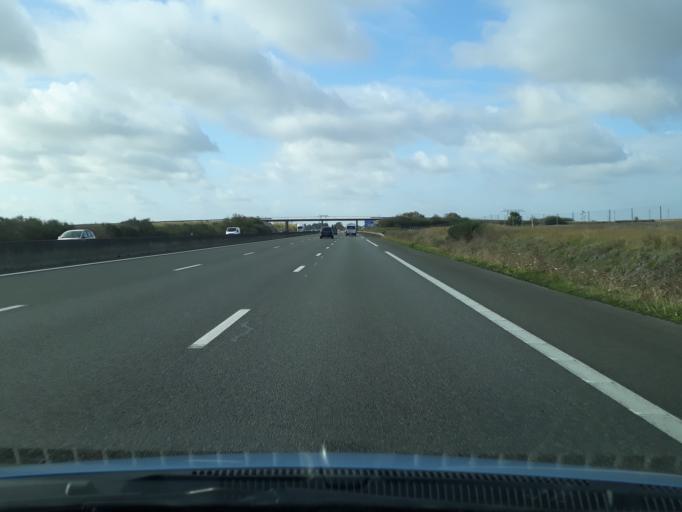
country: FR
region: Centre
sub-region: Departement du Loiret
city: Tavers
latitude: 47.7695
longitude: 1.5716
